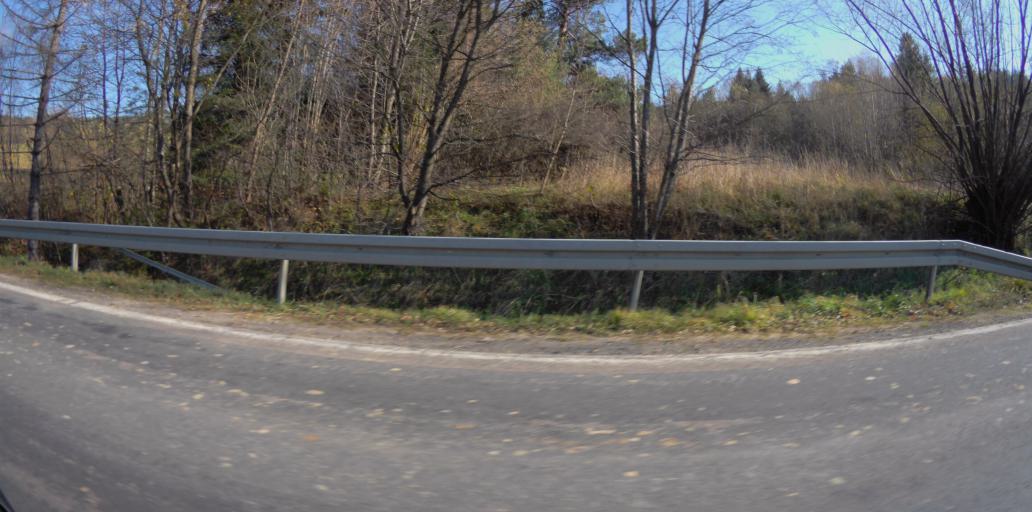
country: PL
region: Subcarpathian Voivodeship
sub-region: Powiat bieszczadzki
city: Ustrzyki Dolne
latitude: 49.5262
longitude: 22.6040
